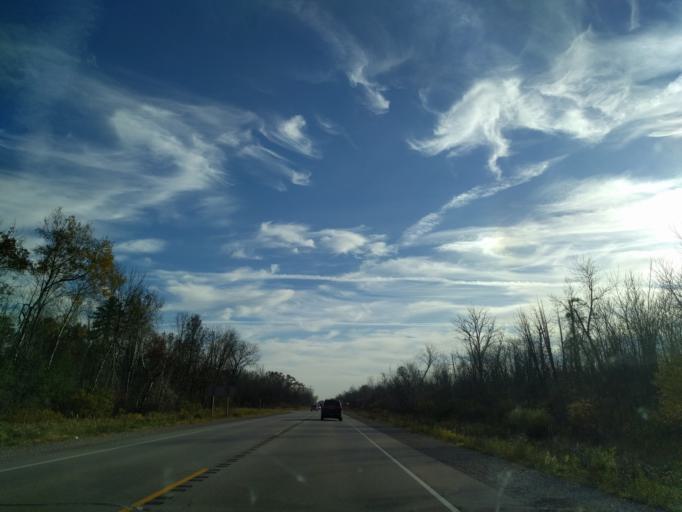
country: US
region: Wisconsin
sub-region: Marinette County
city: Peshtigo
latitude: 45.2424
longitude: -87.9946
